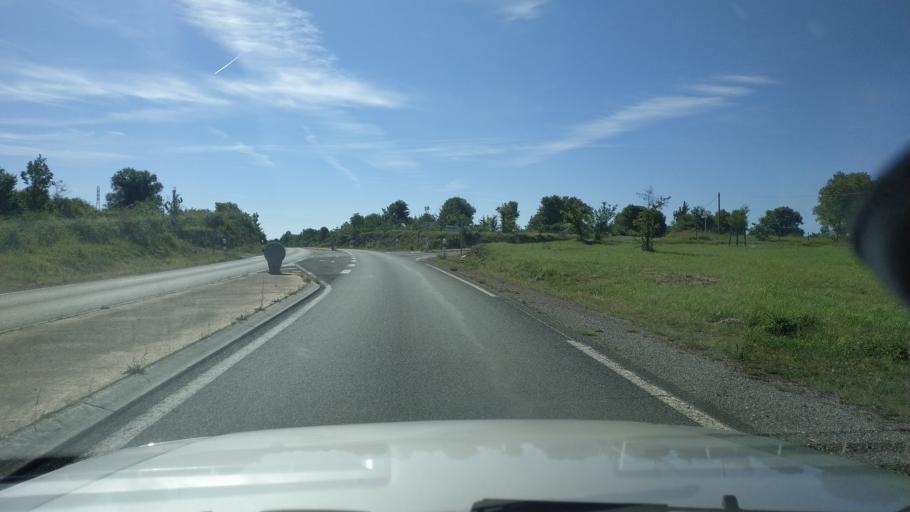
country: FR
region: Midi-Pyrenees
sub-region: Departement du Lot
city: Lacapelle-Marival
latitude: 44.6338
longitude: 1.8648
